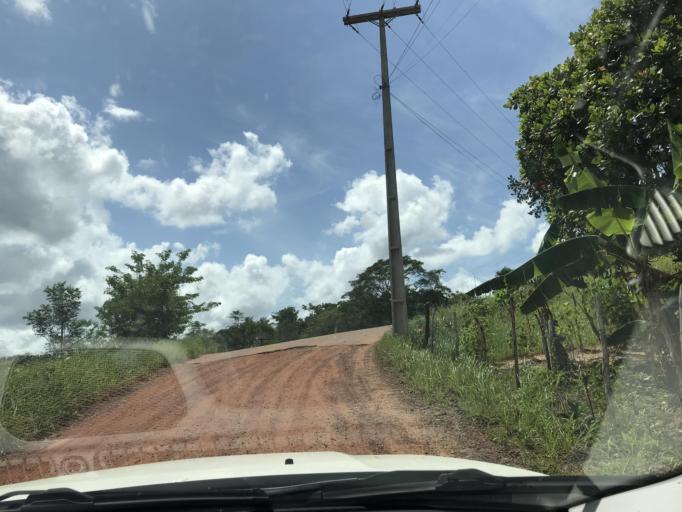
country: BR
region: Bahia
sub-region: Entre Rios
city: Entre Rios
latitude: -12.2417
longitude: -38.0964
